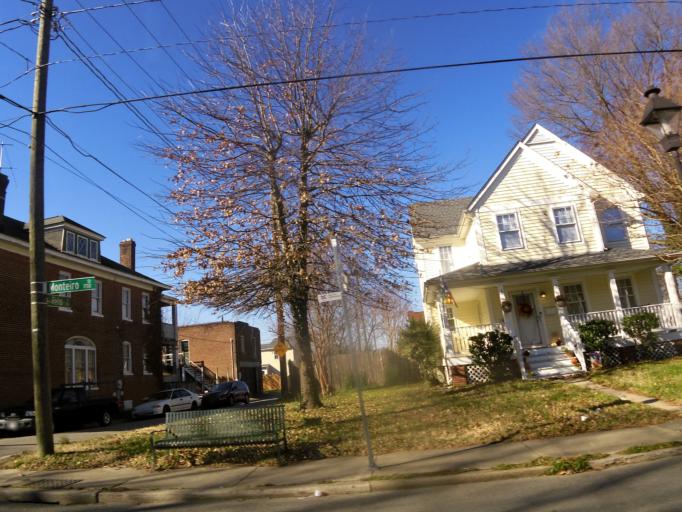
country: US
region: Virginia
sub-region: City of Richmond
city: Richmond
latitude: 37.5575
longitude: -77.4304
